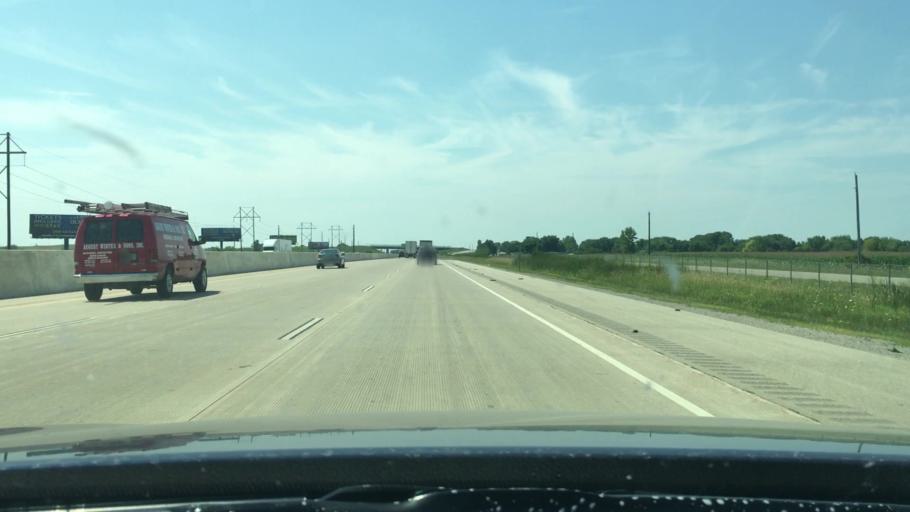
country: US
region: Wisconsin
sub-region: Winnebago County
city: Oshkosh
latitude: 44.0755
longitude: -88.5650
